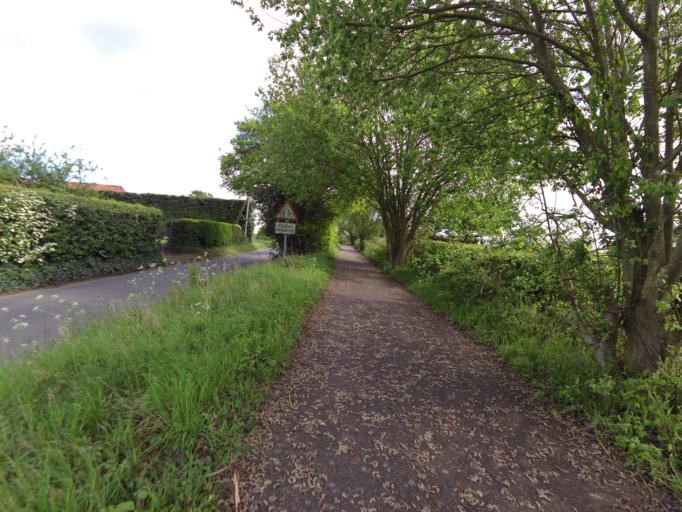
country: GB
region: England
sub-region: Suffolk
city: Woolpit
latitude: 52.2182
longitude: 0.9000
